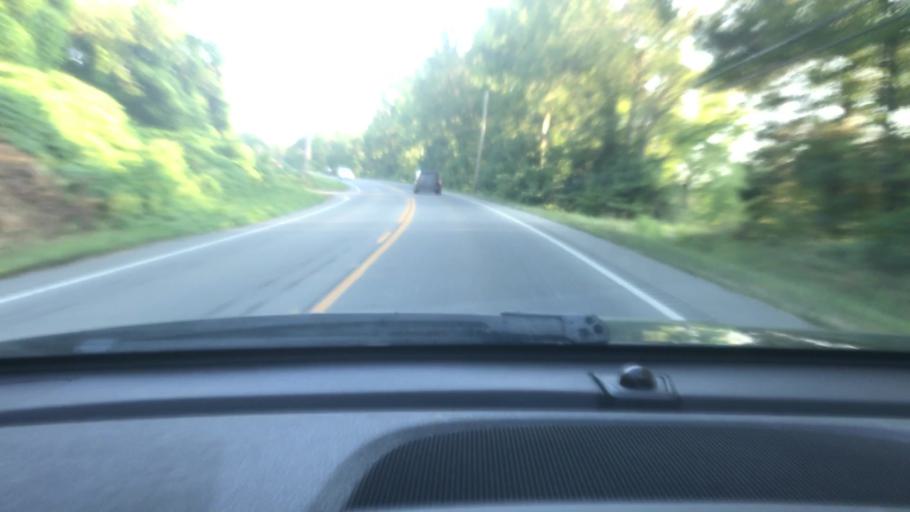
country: US
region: Tennessee
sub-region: Dickson County
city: Charlotte
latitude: 36.1593
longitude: -87.3557
